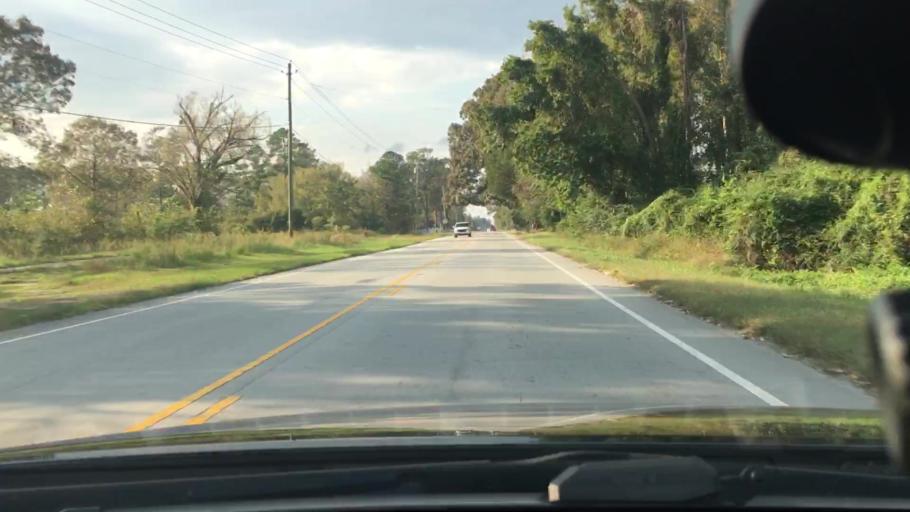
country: US
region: North Carolina
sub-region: Craven County
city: Vanceboro
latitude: 35.2387
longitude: -77.0769
